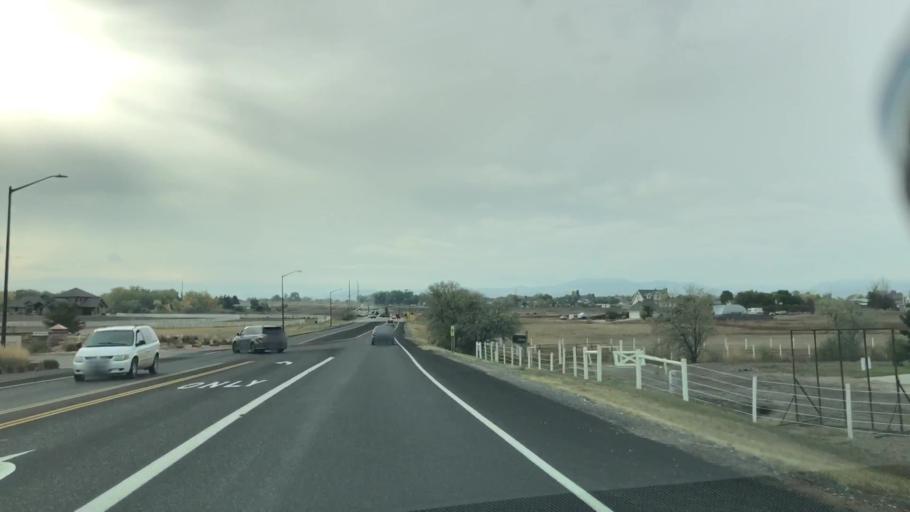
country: US
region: Colorado
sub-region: Larimer County
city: Loveland
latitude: 40.4656
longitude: -105.0345
